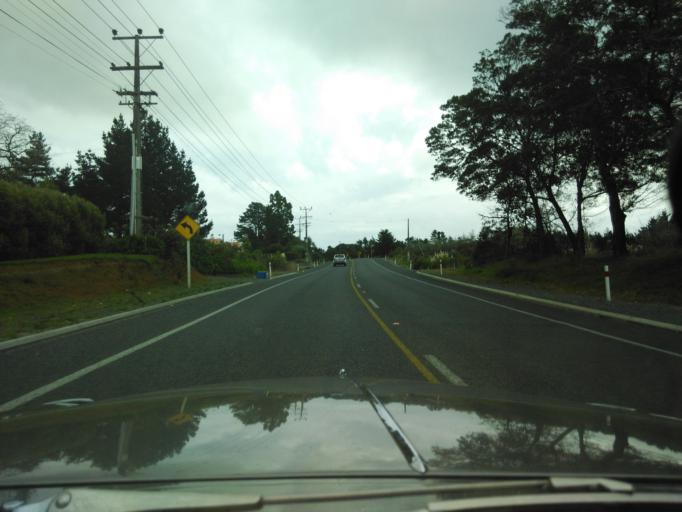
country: NZ
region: Auckland
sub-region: Auckland
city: Muriwai Beach
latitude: -36.7678
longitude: 174.5239
